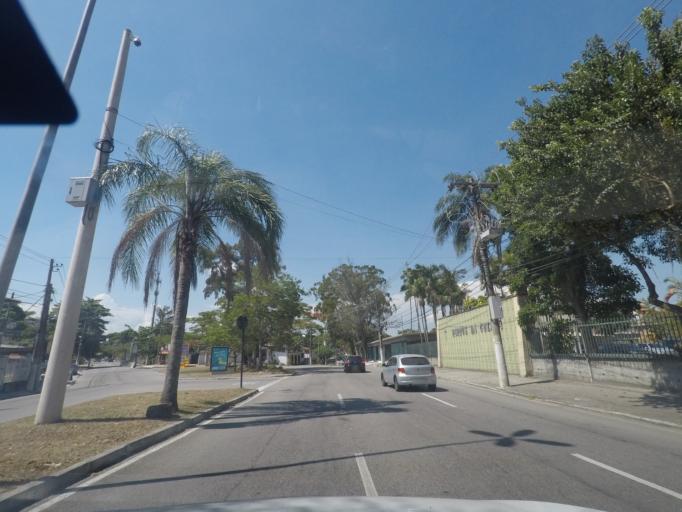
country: BR
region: Rio de Janeiro
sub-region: Niteroi
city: Niteroi
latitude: -22.9129
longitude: -43.0477
